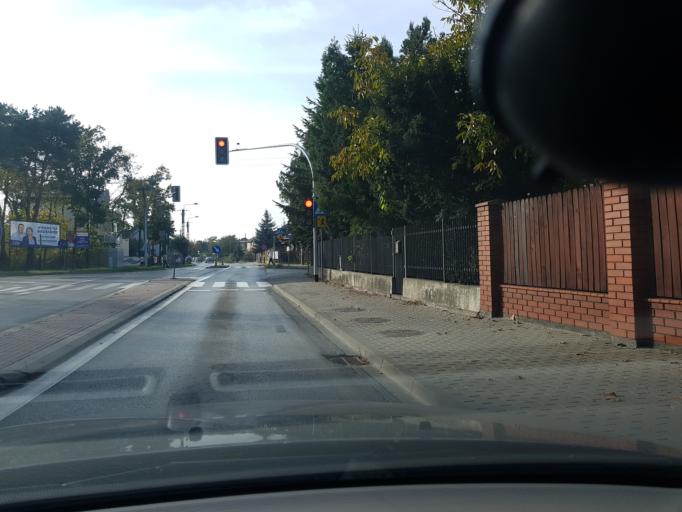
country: PL
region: Masovian Voivodeship
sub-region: Powiat otwocki
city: Otwock
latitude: 52.1066
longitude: 21.2466
